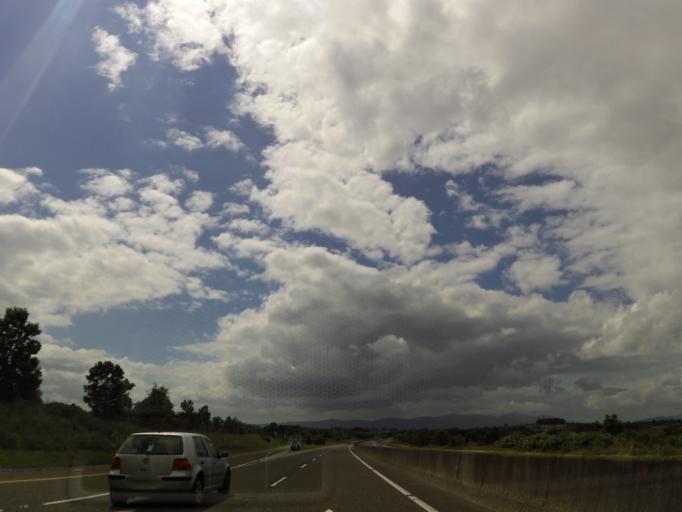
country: IE
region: Munster
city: Cashel
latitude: 52.5131
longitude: -7.8658
